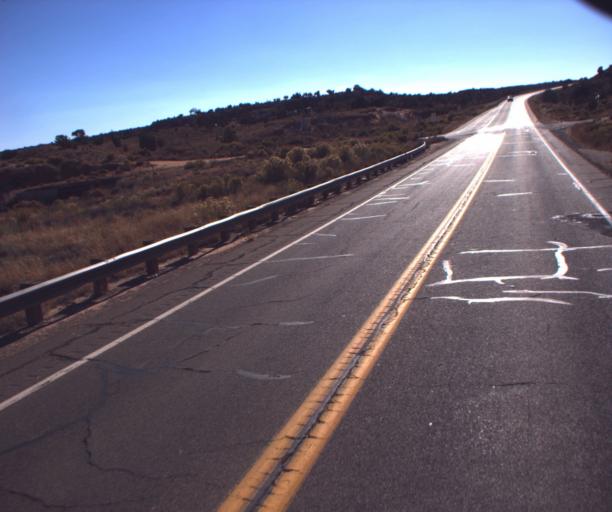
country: US
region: Arizona
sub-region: Coconino County
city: Kaibito
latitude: 36.6101
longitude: -111.0761
